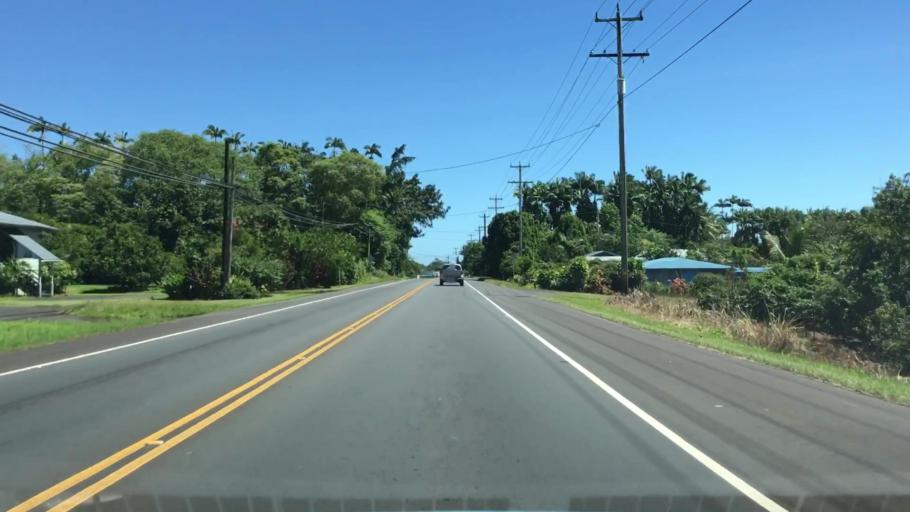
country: US
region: Hawaii
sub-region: Hawaii County
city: Kurtistown
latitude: 19.5973
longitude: -155.0551
